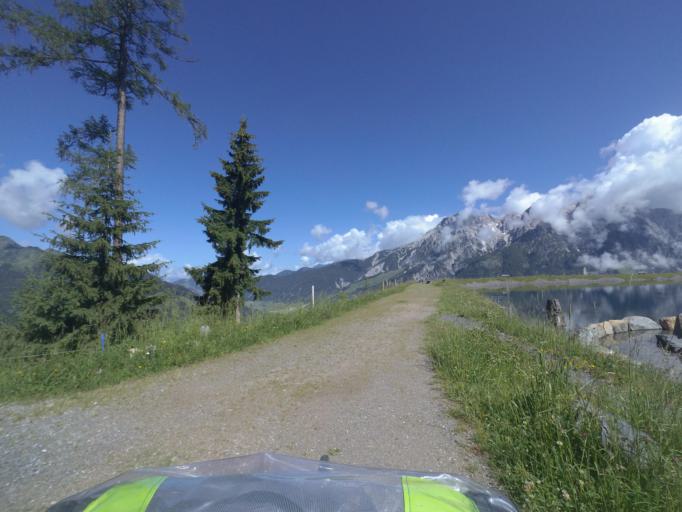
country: AT
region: Salzburg
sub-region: Politischer Bezirk Zell am See
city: Leogang
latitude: 47.4246
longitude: 12.7124
